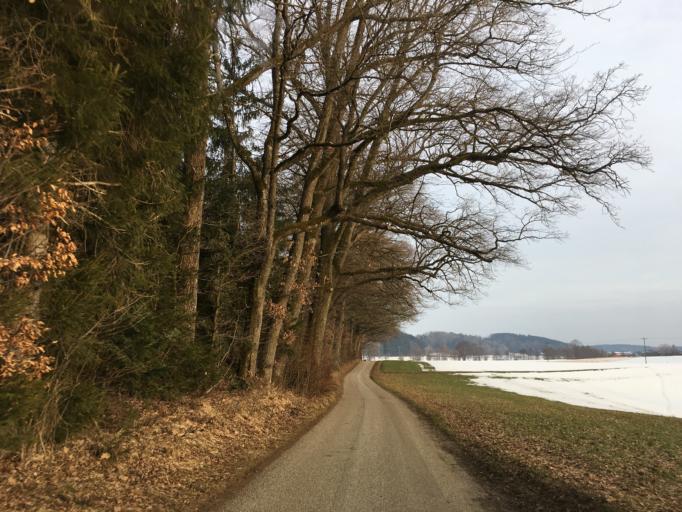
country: DE
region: Bavaria
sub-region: Upper Bavaria
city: Halfing
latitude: 47.9423
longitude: 12.2697
